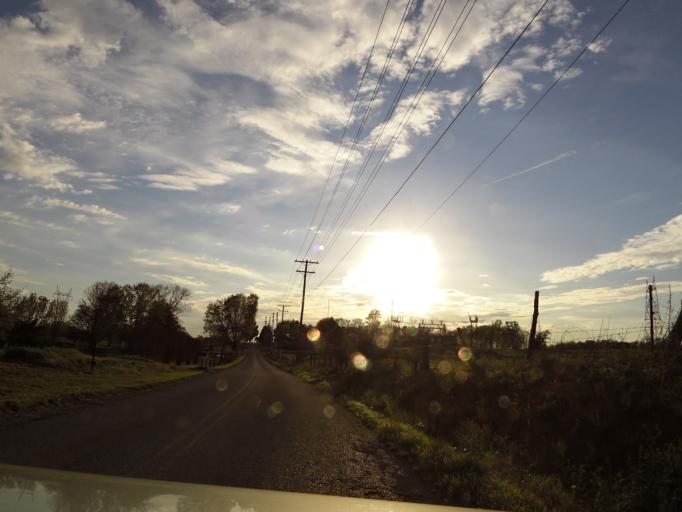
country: US
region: Tennessee
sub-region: Loudon County
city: Greenback
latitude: 35.6304
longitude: -84.0696
